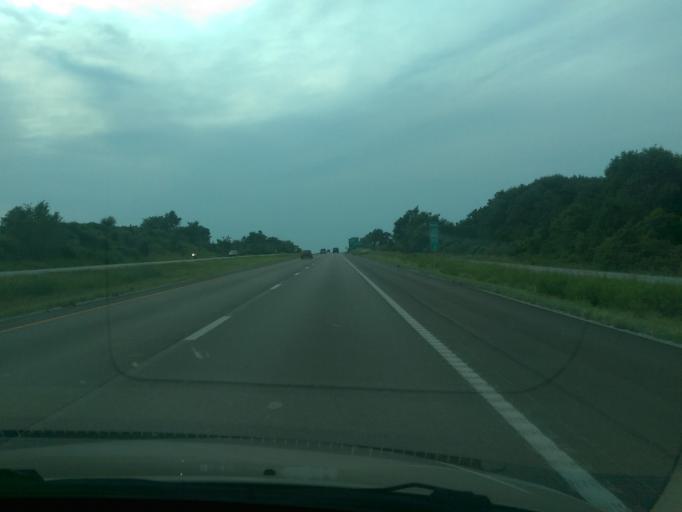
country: US
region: Missouri
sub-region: Andrew County
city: Country Club Village
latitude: 39.8747
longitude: -94.8374
